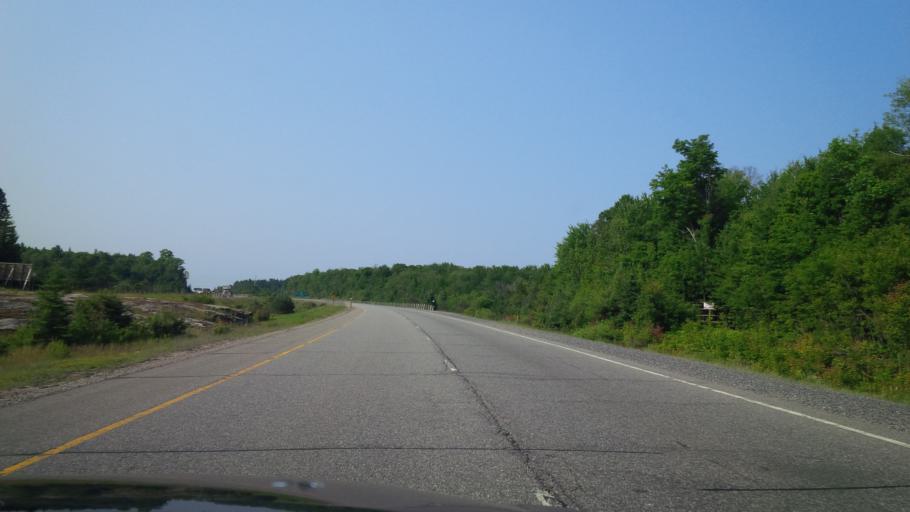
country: CA
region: Ontario
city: Huntsville
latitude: 45.2235
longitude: -79.3122
